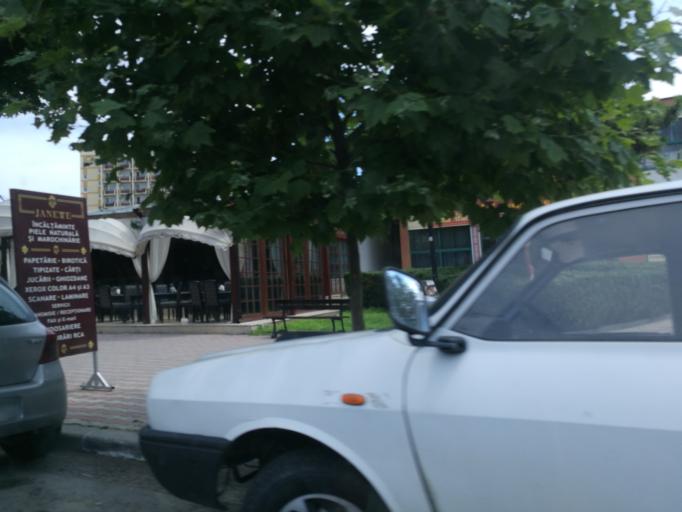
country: RO
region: Constanta
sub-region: Oras Eforie
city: Eforie Nord
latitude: 44.0647
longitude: 28.6342
